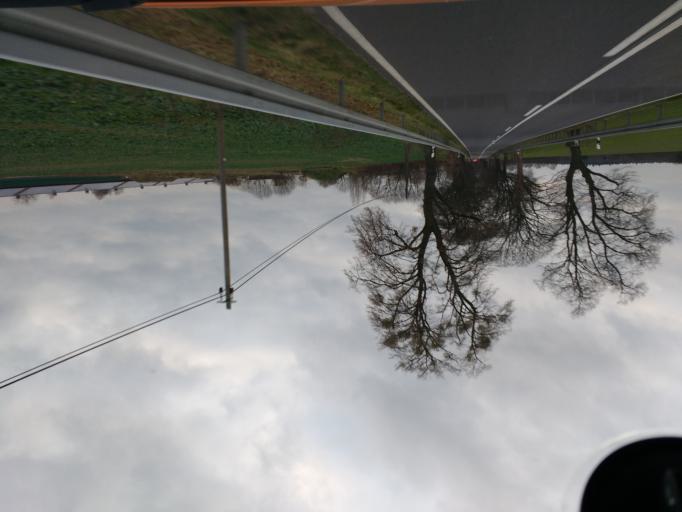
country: DE
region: Brandenburg
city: Protzel
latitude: 52.6411
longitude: 13.9984
